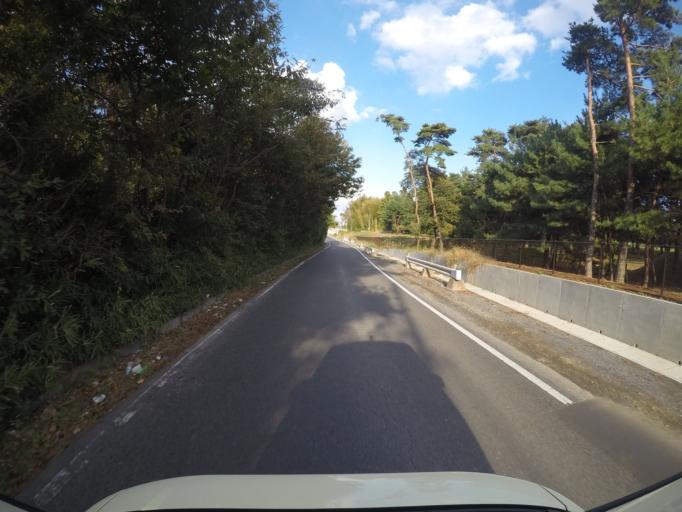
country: JP
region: Ibaraki
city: Mitsukaido
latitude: 36.0110
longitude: 140.0611
